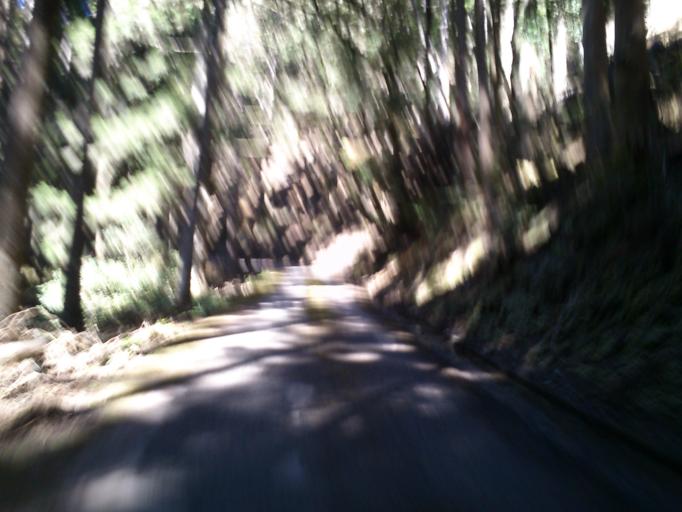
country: JP
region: Kyoto
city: Uji
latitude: 34.8347
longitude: 135.9444
